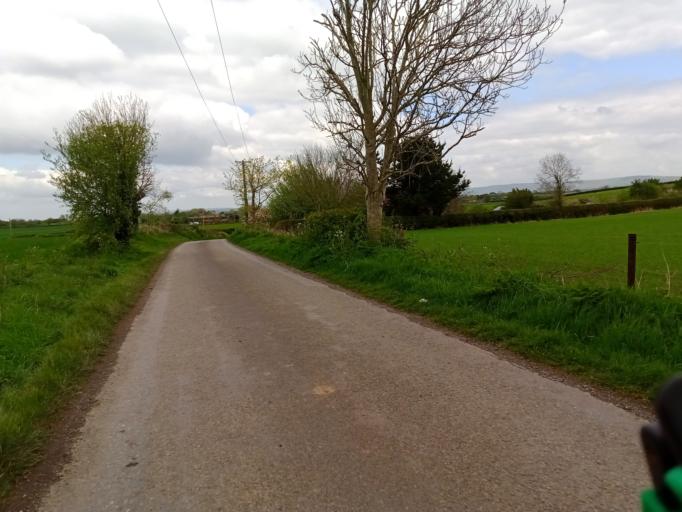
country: IE
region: Leinster
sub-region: Kilkenny
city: Kilkenny
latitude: 52.6265
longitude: -7.2390
